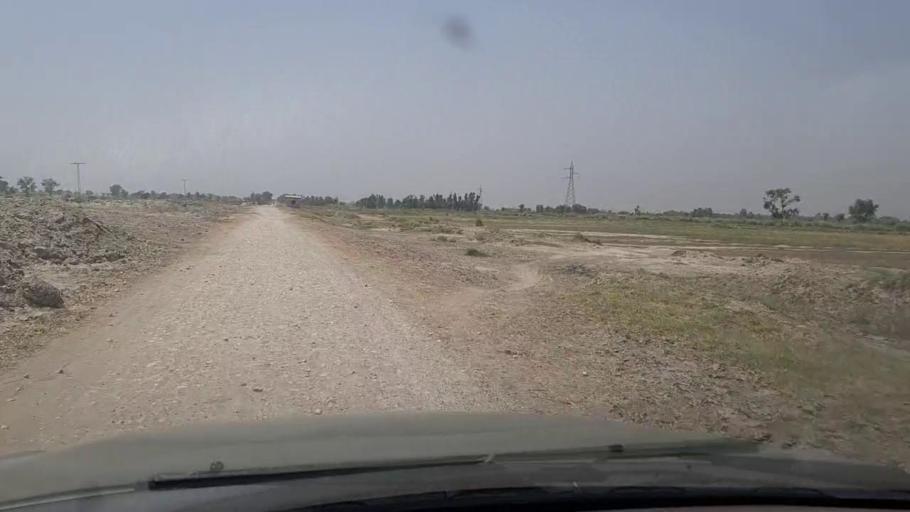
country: PK
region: Sindh
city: Miro Khan
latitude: 27.7789
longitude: 68.1824
